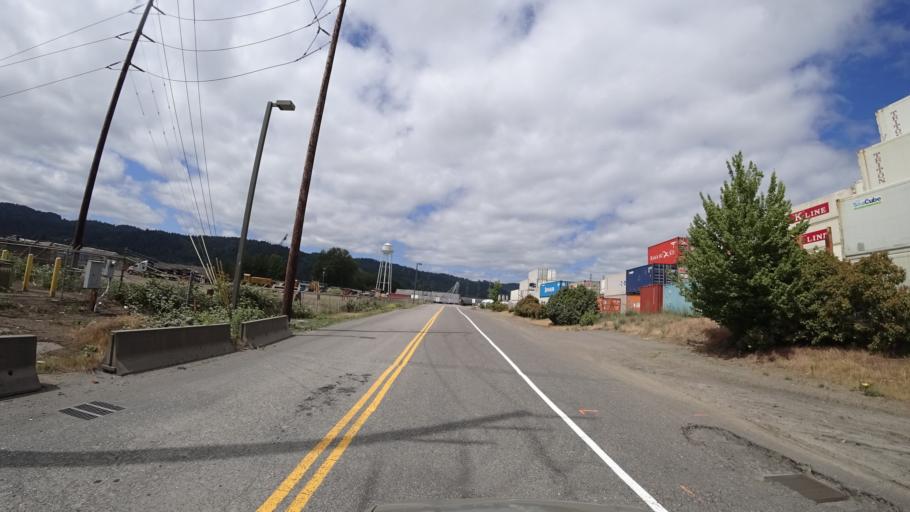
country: US
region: Oregon
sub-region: Washington County
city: West Haven
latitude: 45.6126
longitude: -122.7725
